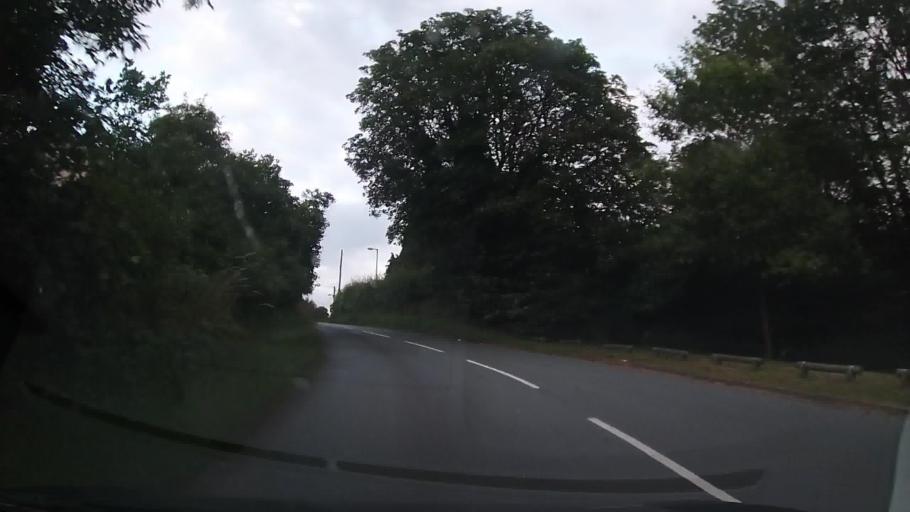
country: GB
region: England
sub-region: Shropshire
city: Petton
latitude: 52.8104
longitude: -2.7864
